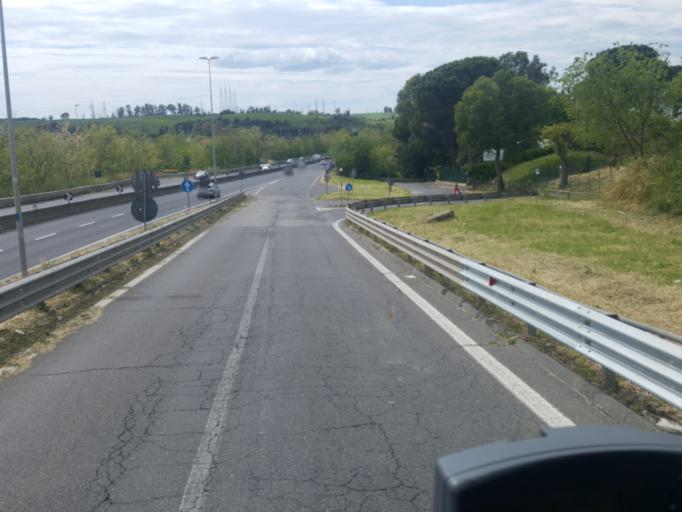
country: IT
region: Latium
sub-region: Citta metropolitana di Roma Capitale
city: La Massimina-Casal Lumbroso
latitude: 41.8828
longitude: 12.3424
